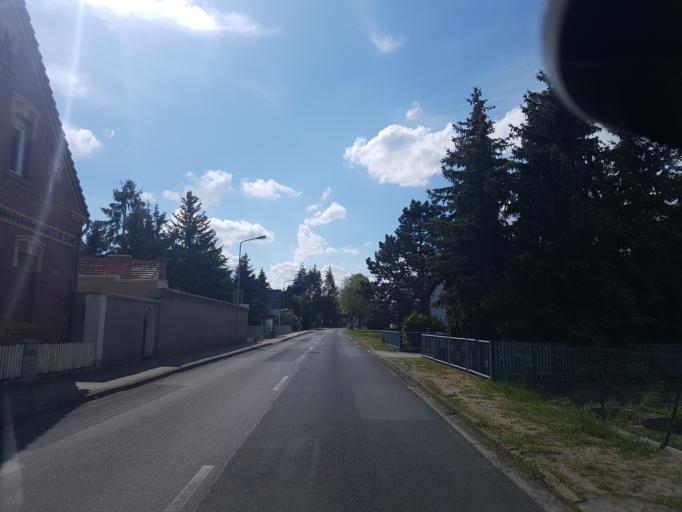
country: DE
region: Brandenburg
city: Spremberg
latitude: 51.6747
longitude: 14.4406
